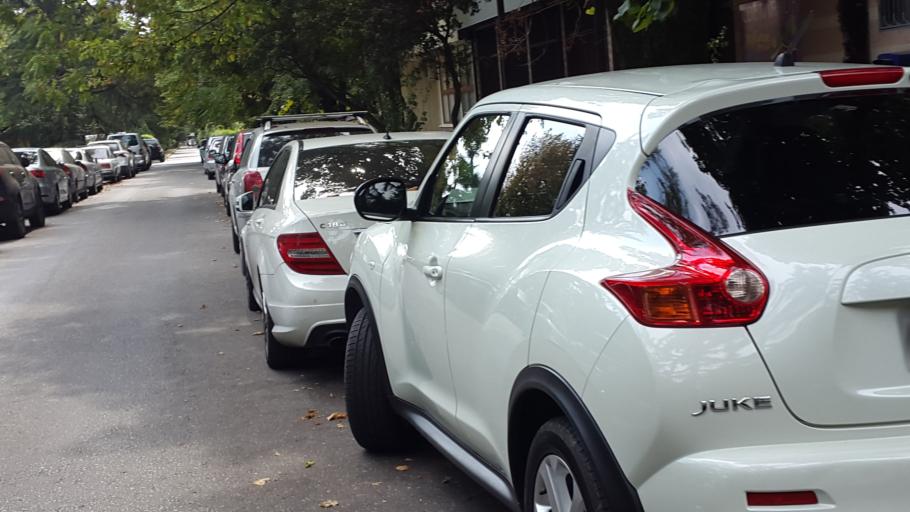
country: RU
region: Krasnodarskiy
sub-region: Sochi City
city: Sochi
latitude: 43.5995
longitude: 39.7238
